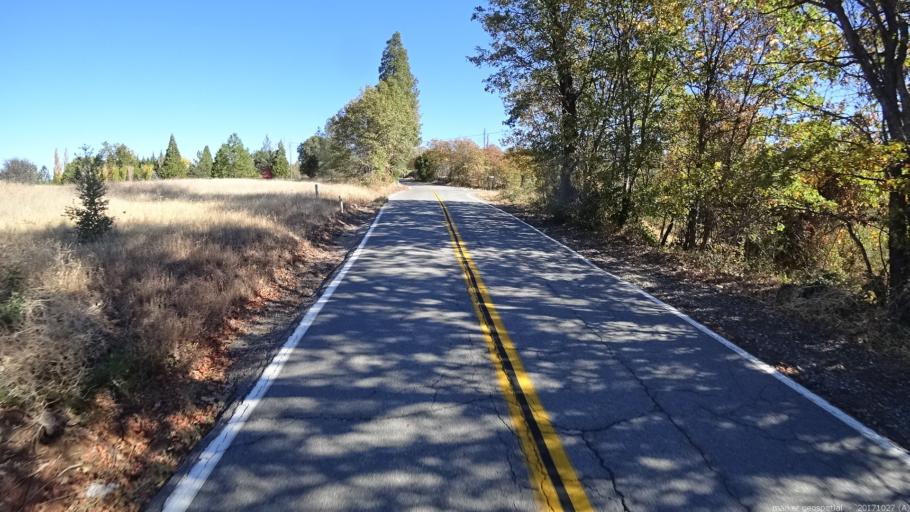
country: US
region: California
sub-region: Shasta County
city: Burney
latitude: 40.7944
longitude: -121.9352
